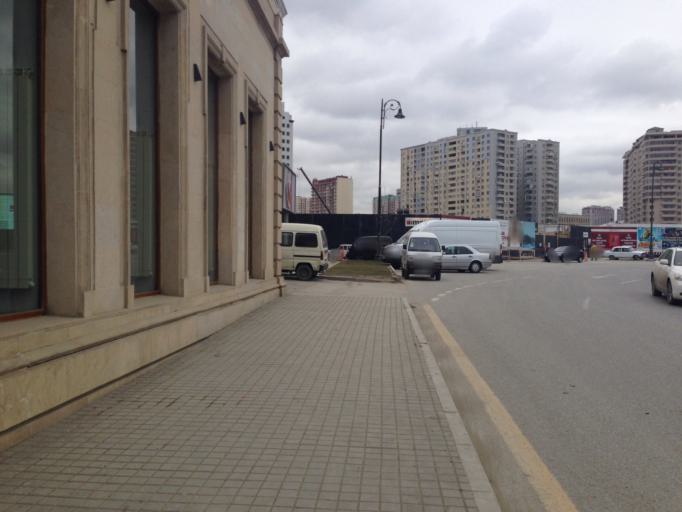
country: AZ
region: Baki
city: Baku
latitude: 40.3875
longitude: 49.8627
